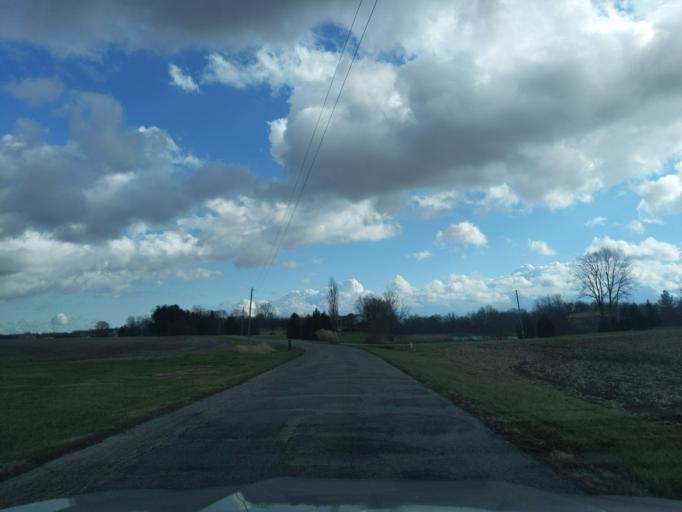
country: US
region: Indiana
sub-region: Decatur County
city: Greensburg
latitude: 39.4094
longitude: -85.5225
